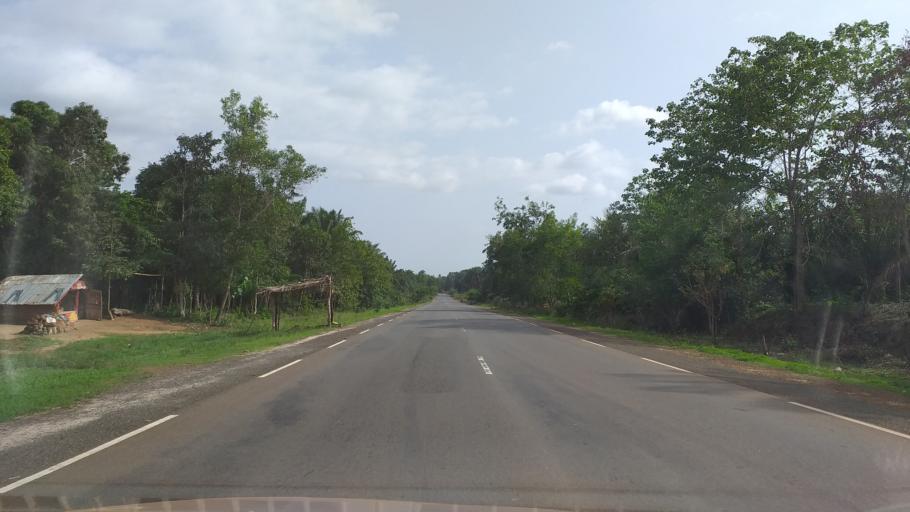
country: GN
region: Boke
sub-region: Boke Prefecture
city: Sangueya
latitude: 10.5719
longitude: -14.3965
